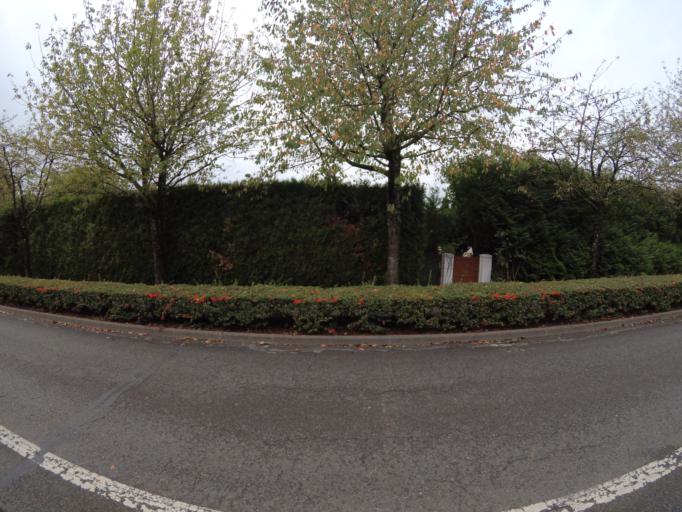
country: FR
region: Ile-de-France
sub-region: Departement de Seine-et-Marne
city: Montevrain
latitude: 48.8744
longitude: 2.7512
